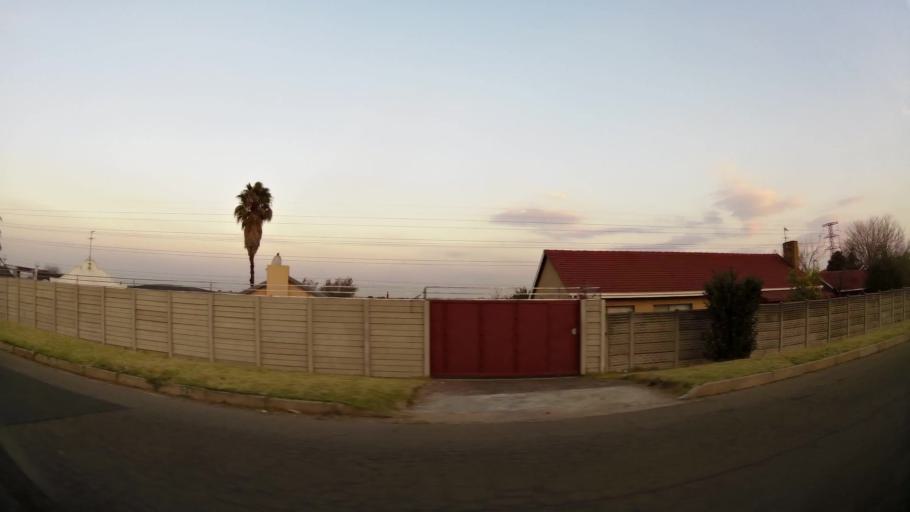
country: ZA
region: Gauteng
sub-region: Ekurhuleni Metropolitan Municipality
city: Tembisa
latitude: -26.0609
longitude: 28.2393
